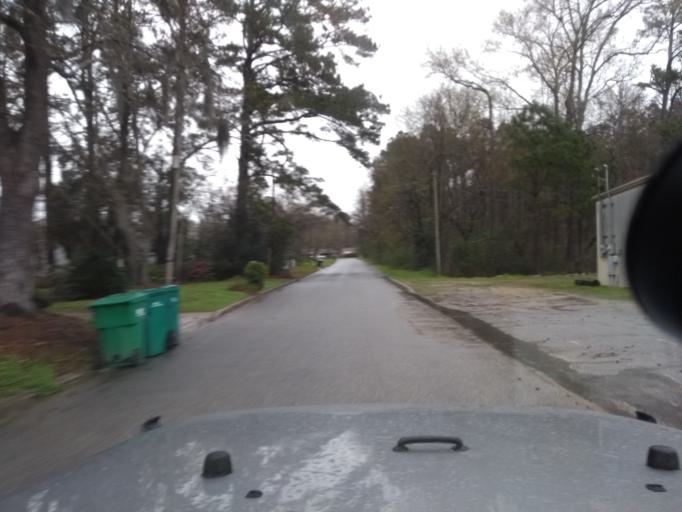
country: US
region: Georgia
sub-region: Chatham County
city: Garden City
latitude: 32.0889
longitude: -81.1570
